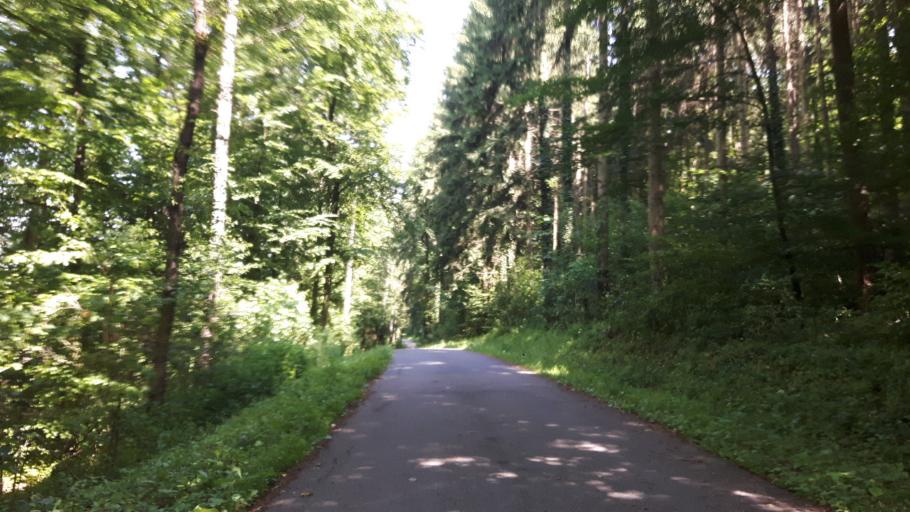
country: DE
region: Baden-Wuerttemberg
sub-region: Regierungsbezirk Stuttgart
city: Forchtenberg
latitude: 49.3387
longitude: 9.5385
